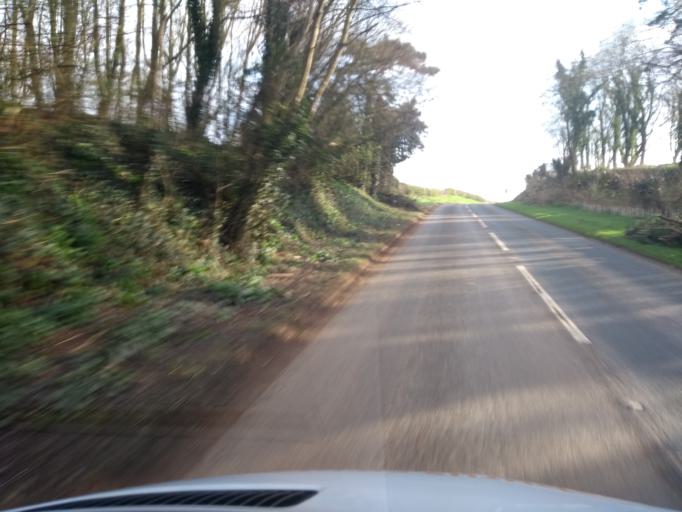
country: GB
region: England
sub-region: Somerset
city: Castle Cary
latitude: 51.0764
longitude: -2.5116
